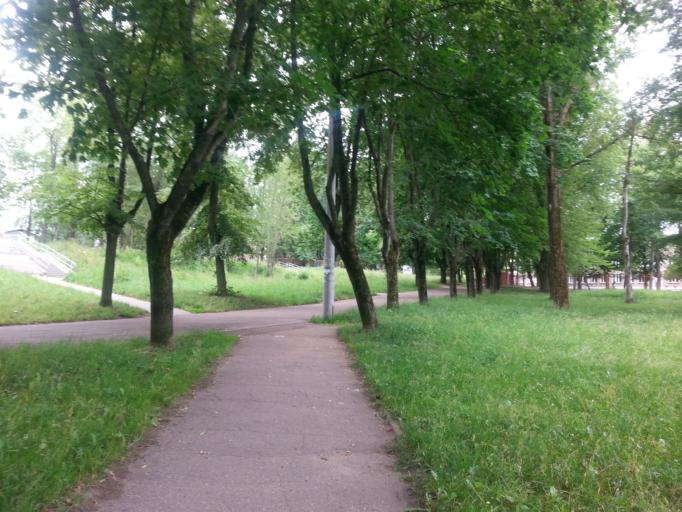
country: BY
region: Minsk
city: Novoye Medvezhino
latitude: 53.8998
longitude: 27.5007
